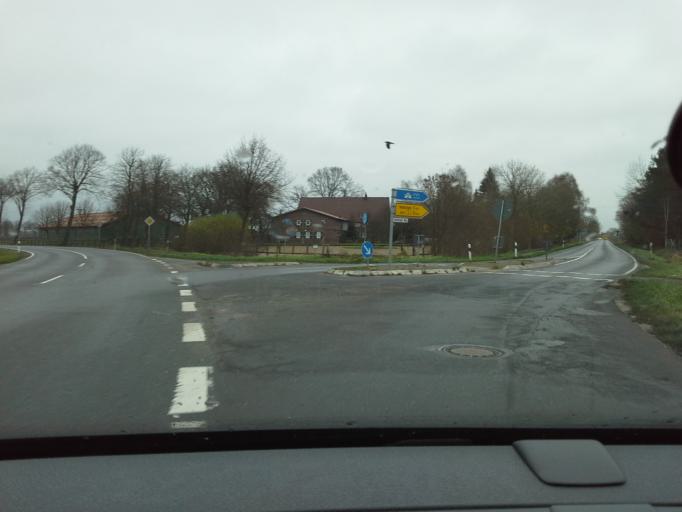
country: DE
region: Schleswig-Holstein
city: Ellerhoop
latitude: 53.7320
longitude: 9.7725
